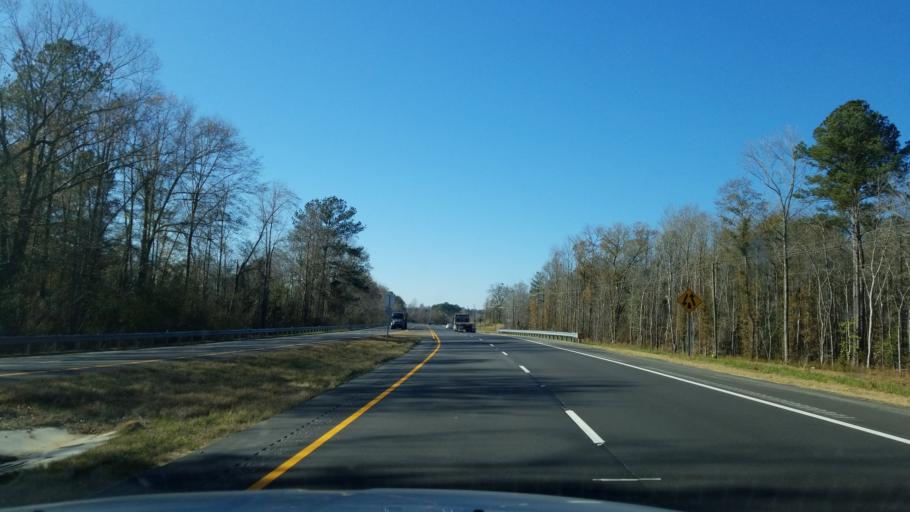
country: US
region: Alabama
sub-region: Pickens County
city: Reform
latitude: 33.3714
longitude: -87.9915
